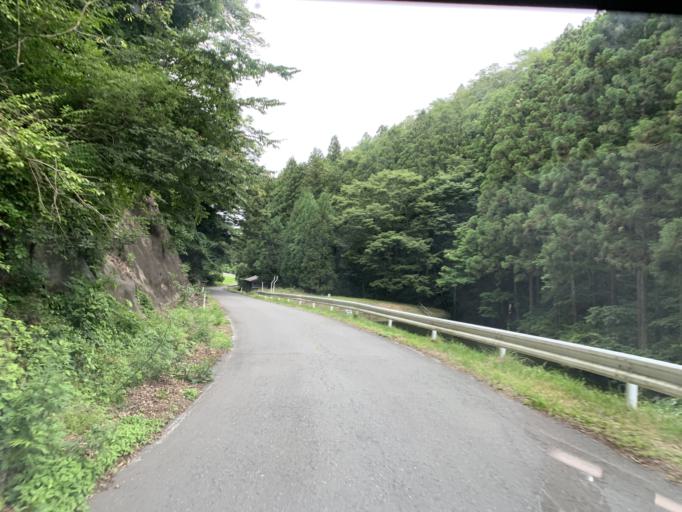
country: JP
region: Iwate
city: Ichinoseki
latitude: 38.8304
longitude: 141.2399
